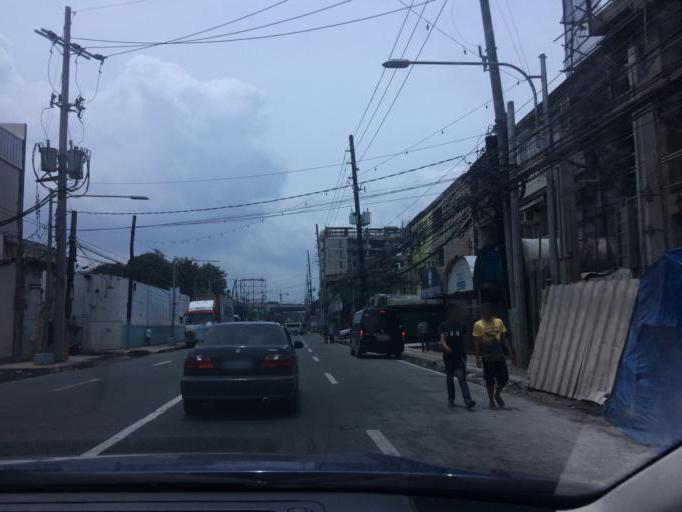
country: PH
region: Metro Manila
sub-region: Makati City
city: Makati City
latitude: 14.5204
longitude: 120.9966
